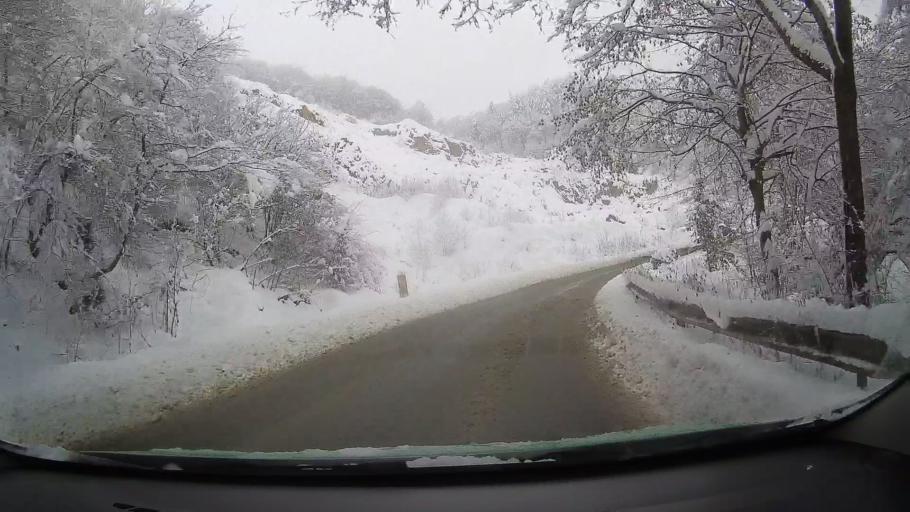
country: RO
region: Sibiu
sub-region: Comuna Tilisca
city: Tilisca
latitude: 45.8021
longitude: 23.8097
